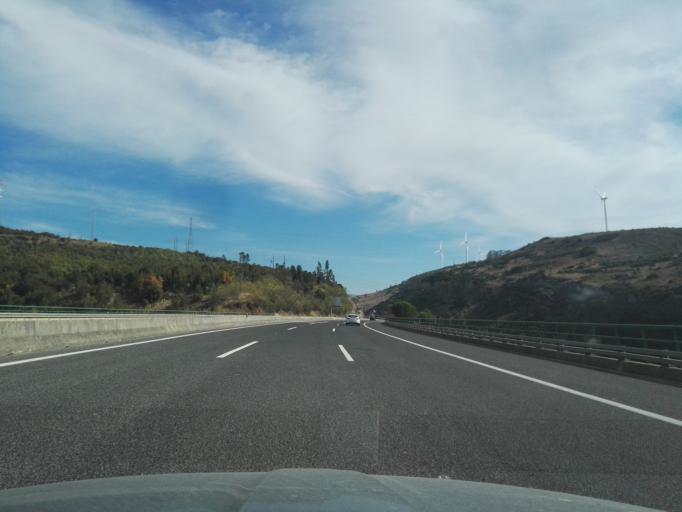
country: PT
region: Lisbon
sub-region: Loures
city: Santo Antao do Tojal
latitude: 38.8753
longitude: -9.1338
